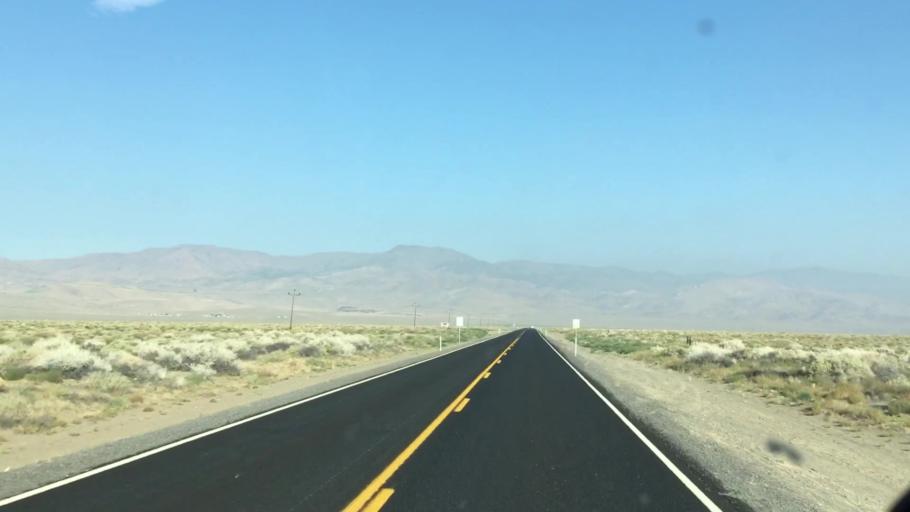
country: US
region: Nevada
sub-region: Lyon County
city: Fernley
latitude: 39.6423
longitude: -119.3024
